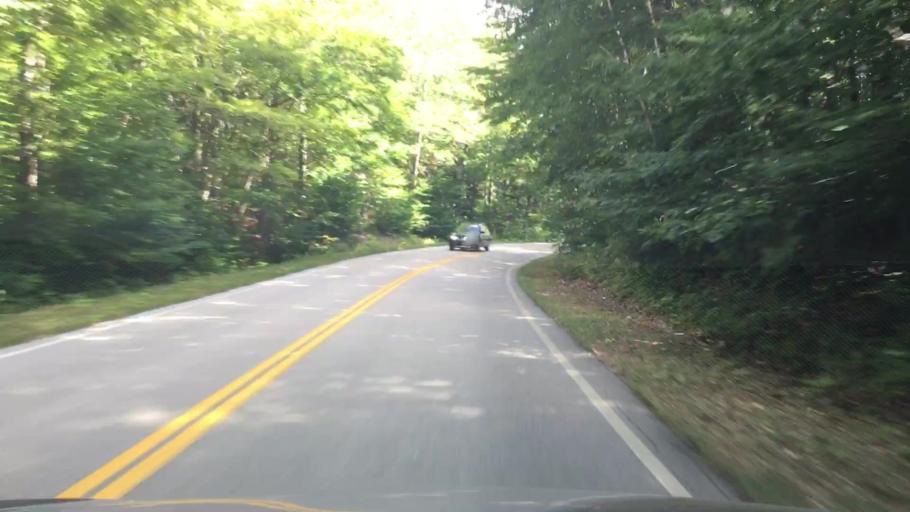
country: US
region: New Hampshire
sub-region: Carroll County
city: Tamworth
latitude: 44.0273
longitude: -71.3218
